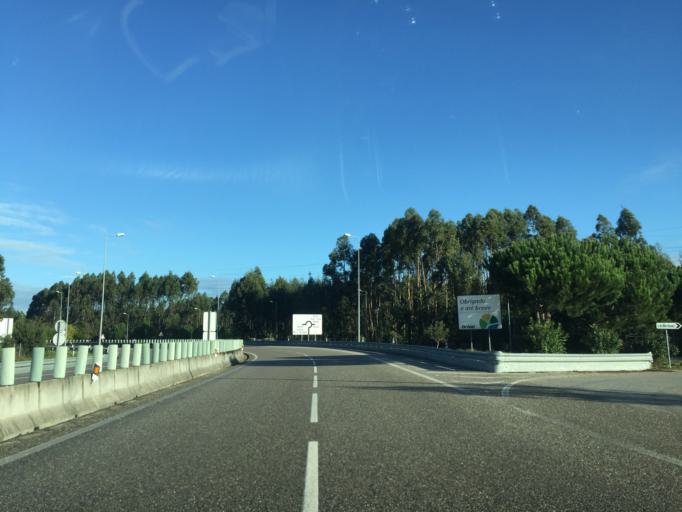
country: PT
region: Coimbra
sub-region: Figueira da Foz
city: Lavos
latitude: 40.0483
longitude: -8.8144
